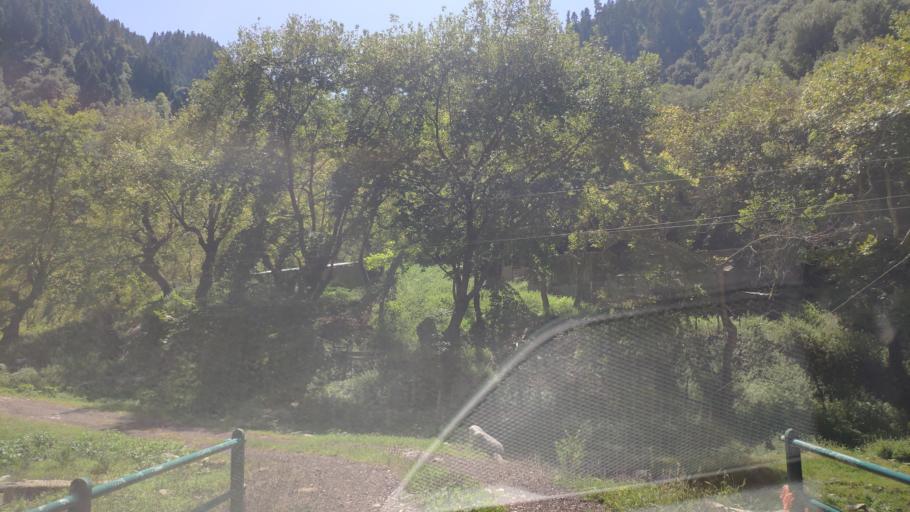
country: GR
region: Central Greece
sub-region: Nomos Evrytanias
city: Kerasochori
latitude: 39.1248
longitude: 21.6553
